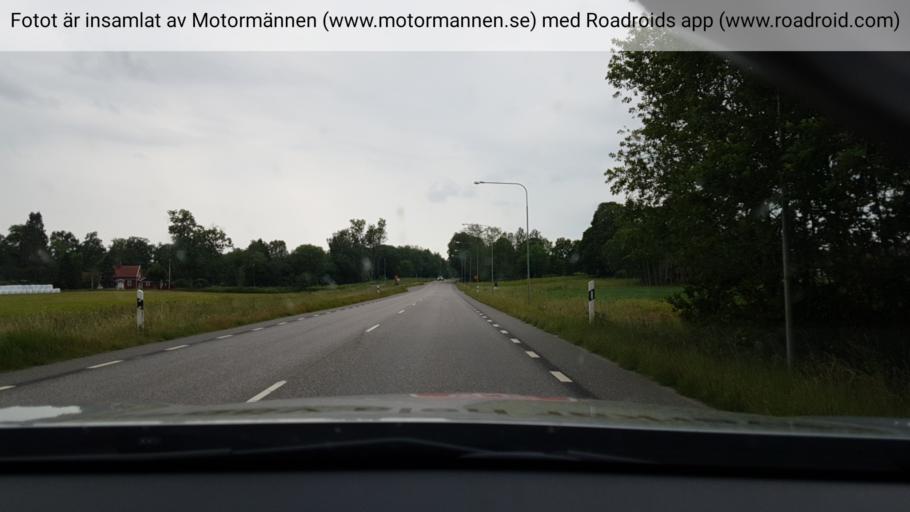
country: SE
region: Vaestra Goetaland
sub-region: Tidaholms Kommun
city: Tidaholm
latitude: 58.1602
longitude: 13.9308
